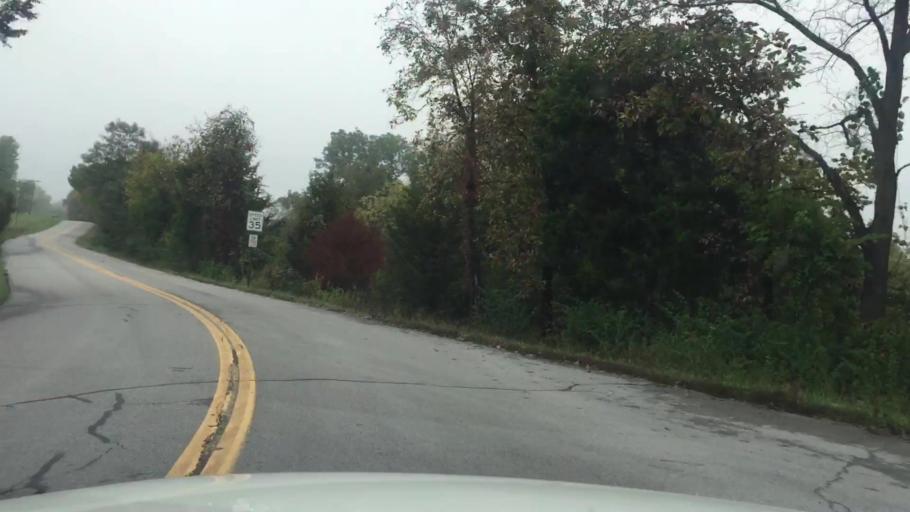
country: US
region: Missouri
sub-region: Boone County
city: Ashland
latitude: 38.8558
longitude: -92.3059
